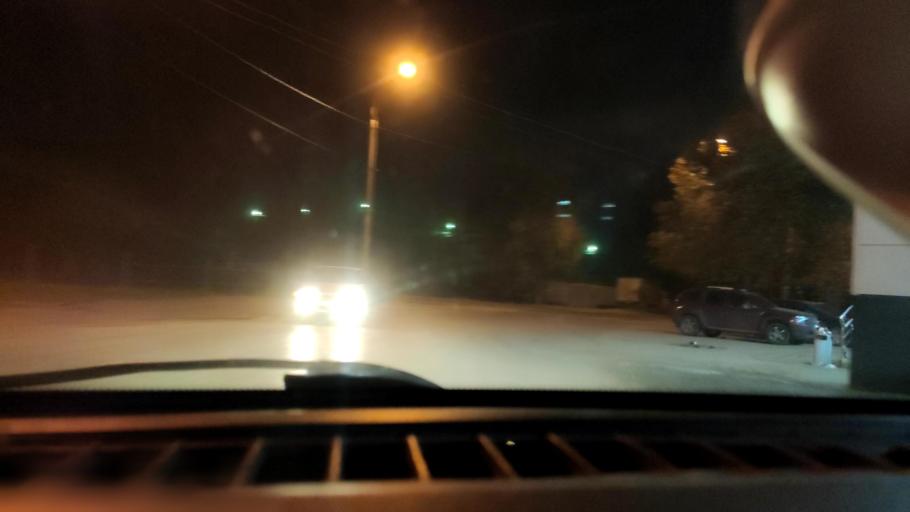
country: RU
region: Samara
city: Samara
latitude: 53.1992
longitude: 50.2494
